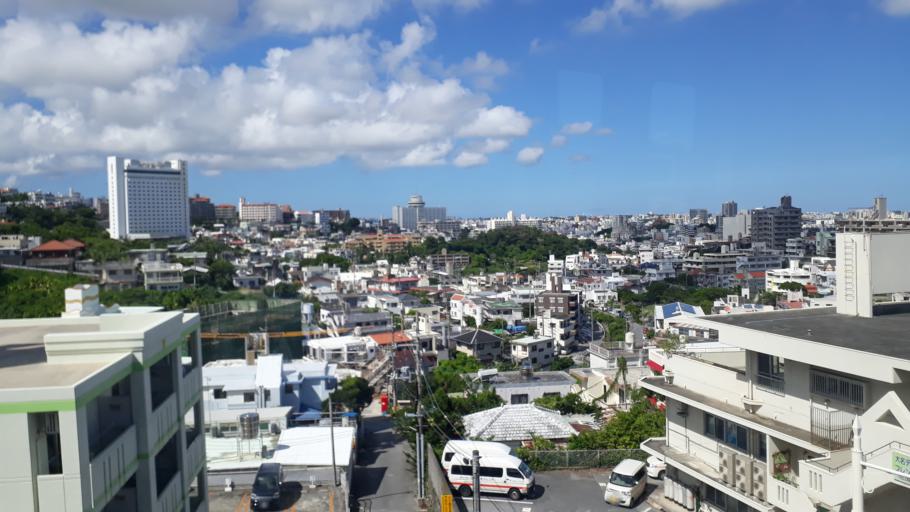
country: JP
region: Okinawa
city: Naha-shi
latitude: 26.2261
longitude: 127.7103
